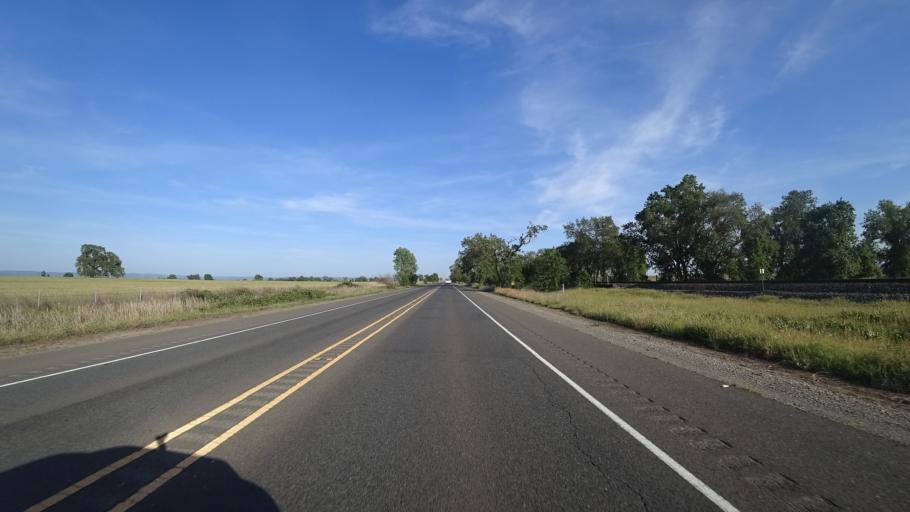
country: US
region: California
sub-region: Placer County
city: Sheridan
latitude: 38.9307
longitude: -121.3424
